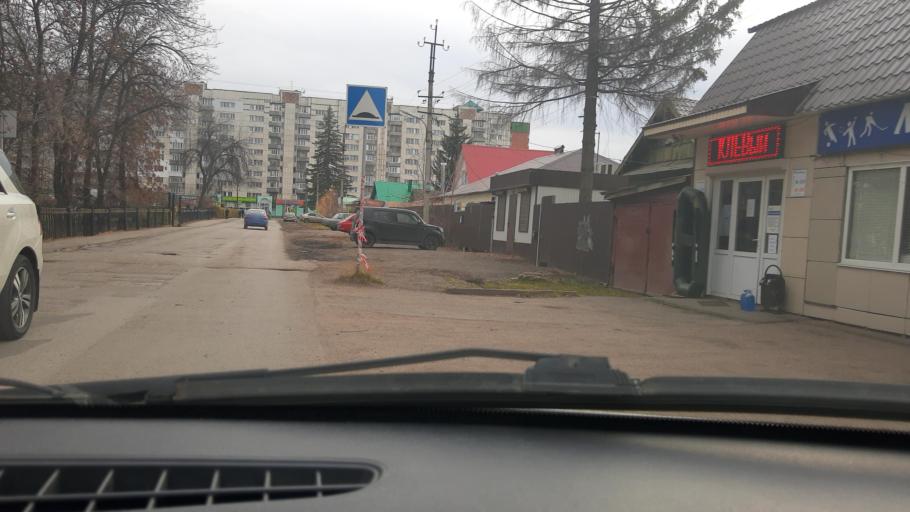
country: RU
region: Bashkortostan
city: Avdon
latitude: 54.7034
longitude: 55.8256
